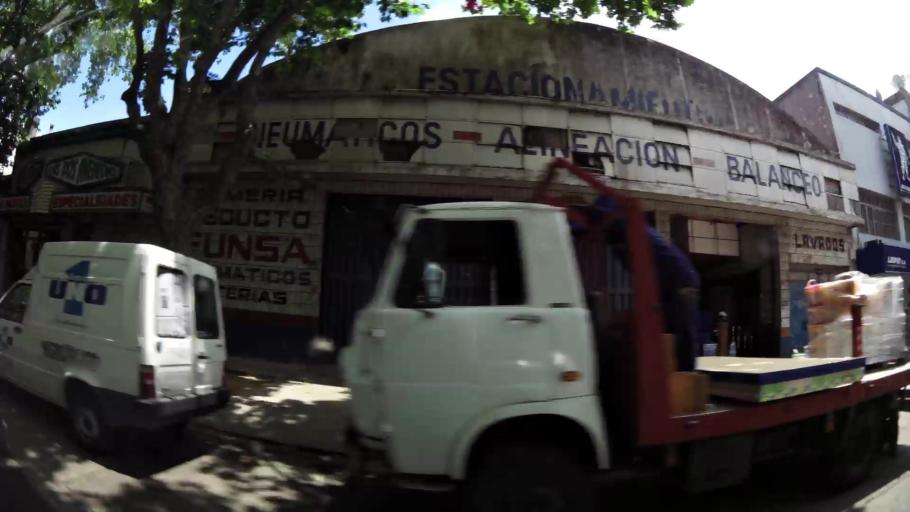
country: UY
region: Montevideo
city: Montevideo
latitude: -34.8737
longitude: -56.1838
